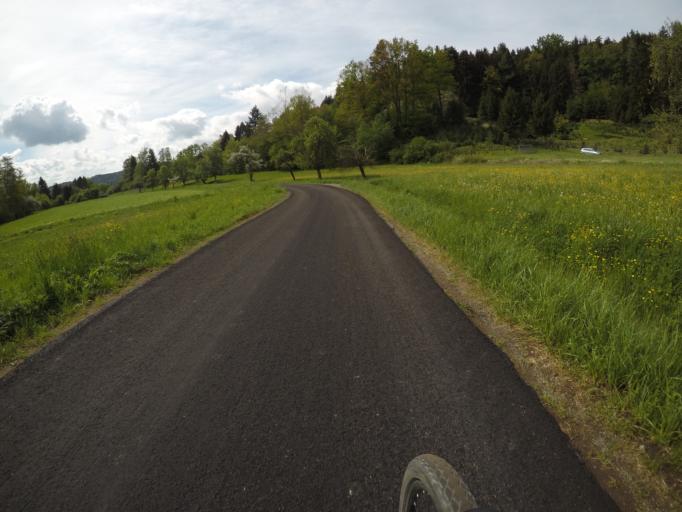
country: DE
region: Baden-Wuerttemberg
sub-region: Tuebingen Region
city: Tuebingen
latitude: 48.5295
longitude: 9.0067
